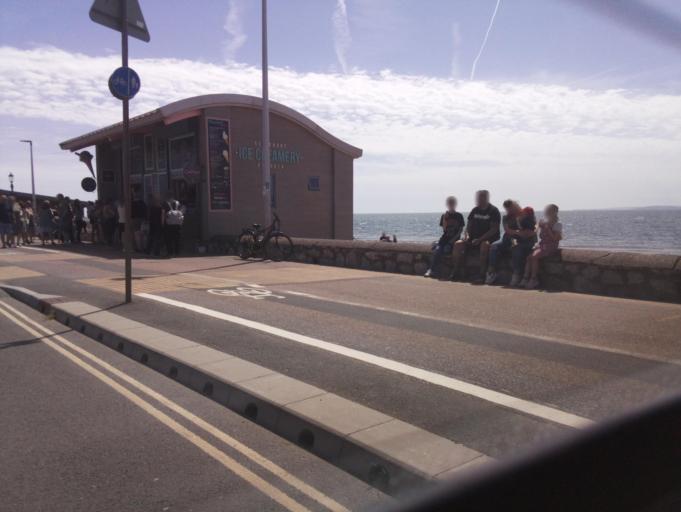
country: GB
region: England
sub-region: Devon
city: Exmouth
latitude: 50.6129
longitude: -3.4096
